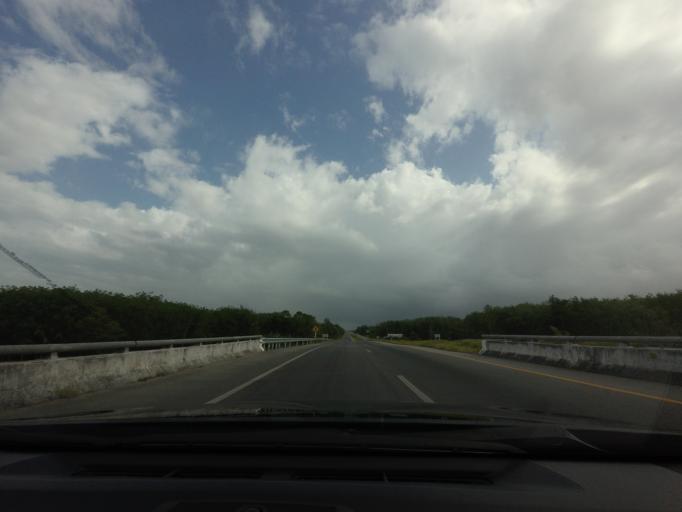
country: TH
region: Pattani
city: Mae Lan
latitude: 6.6848
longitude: 101.2314
